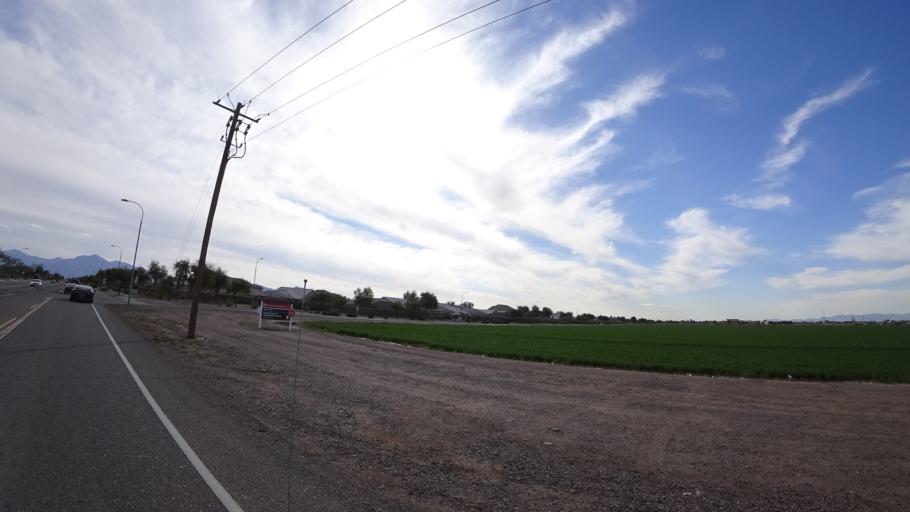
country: US
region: Arizona
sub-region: Maricopa County
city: Tolleson
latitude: 33.4290
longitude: -112.2725
